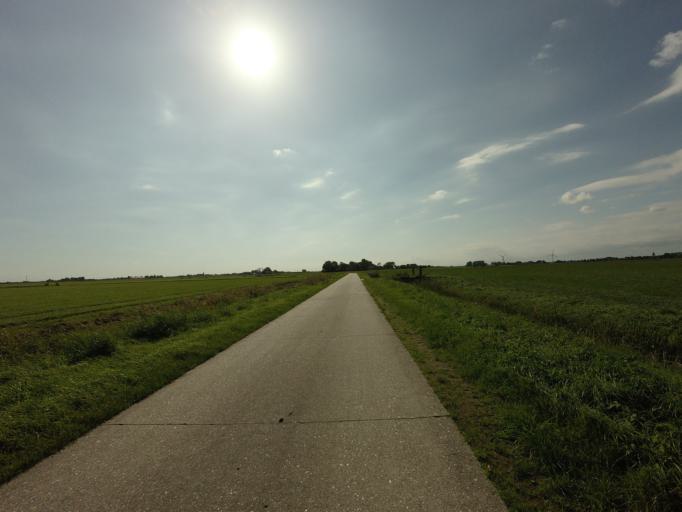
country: NL
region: Friesland
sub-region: Gemeente Littenseradiel
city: Makkum
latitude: 53.0967
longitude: 5.6470
